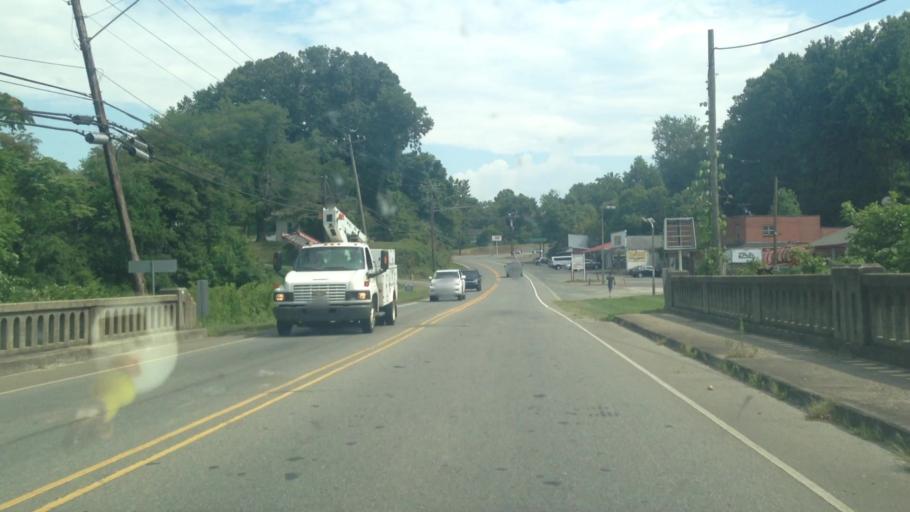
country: US
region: North Carolina
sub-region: Surry County
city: Mount Airy
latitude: 36.4913
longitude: -80.5954
